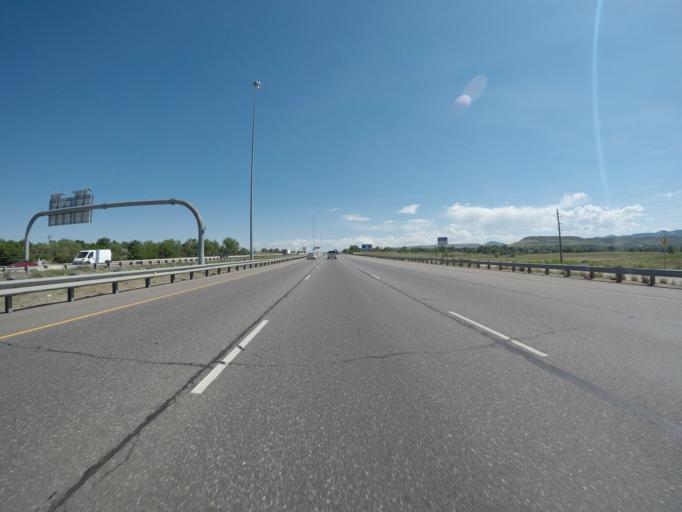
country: US
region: Colorado
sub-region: Jefferson County
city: Applewood
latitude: 39.7711
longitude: -105.1434
